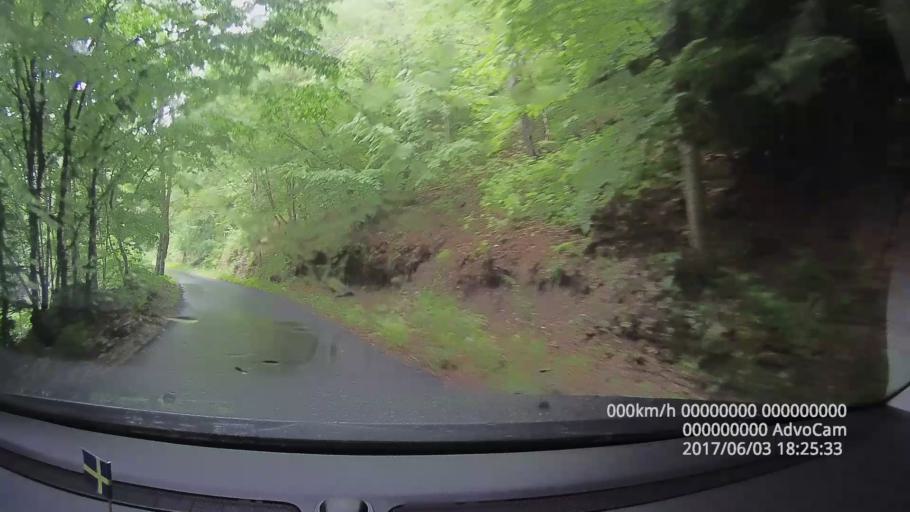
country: RO
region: Gorj
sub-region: Comuna Runcu
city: Dobrita
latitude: 45.1743
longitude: 23.1922
